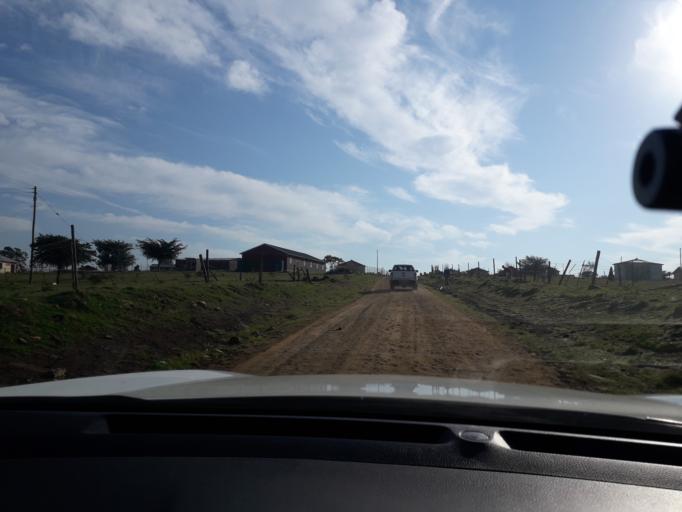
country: ZA
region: Eastern Cape
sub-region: Buffalo City Metropolitan Municipality
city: Bhisho
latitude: -32.9391
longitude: 27.2900
